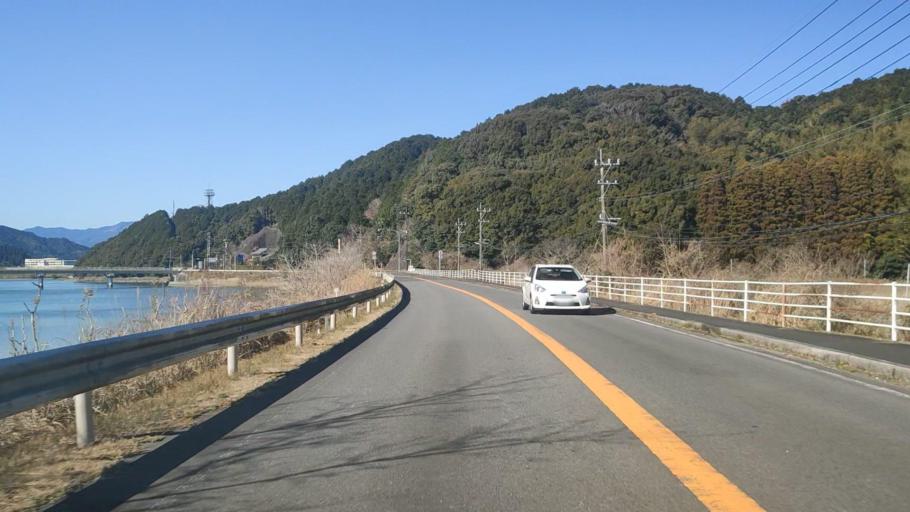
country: JP
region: Oita
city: Saiki
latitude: 32.9399
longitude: 131.9140
